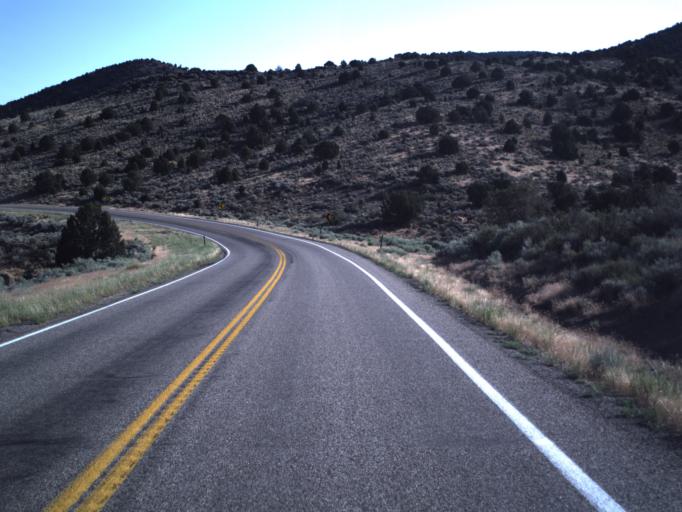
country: US
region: Utah
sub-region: Iron County
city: Parowan
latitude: 38.1069
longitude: -112.9470
